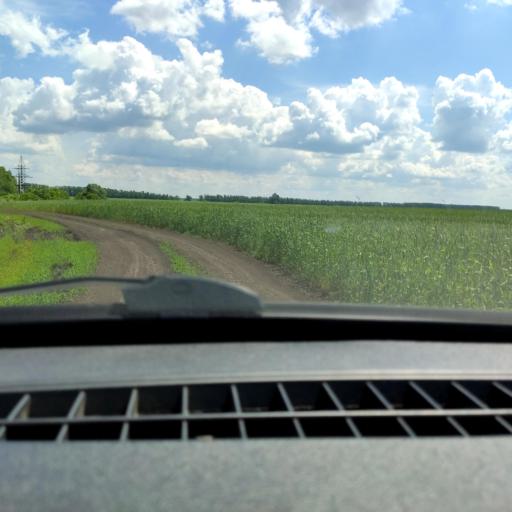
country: RU
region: Bashkortostan
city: Kabakovo
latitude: 54.5238
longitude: 56.0660
